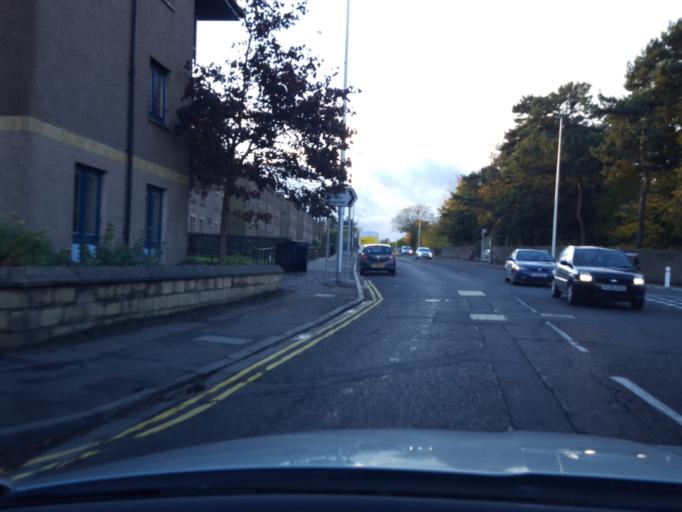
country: GB
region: Scotland
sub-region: Dundee City
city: Dundee
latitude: 56.4751
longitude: -2.9845
